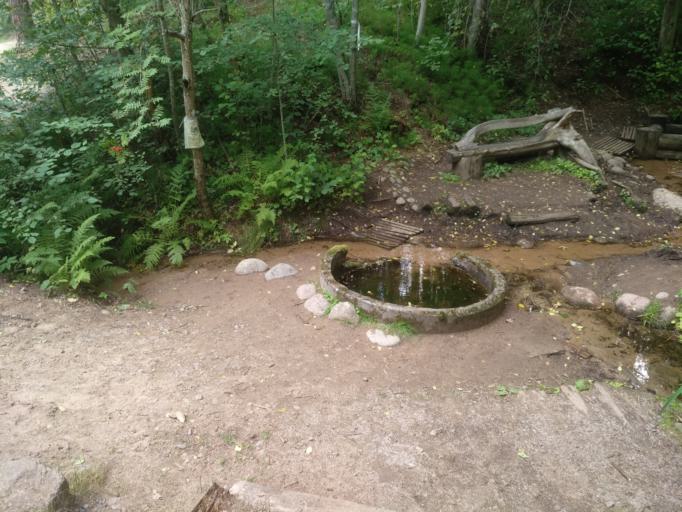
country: RU
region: Leningrad
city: Sapernoye
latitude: 60.6762
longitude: 29.9268
